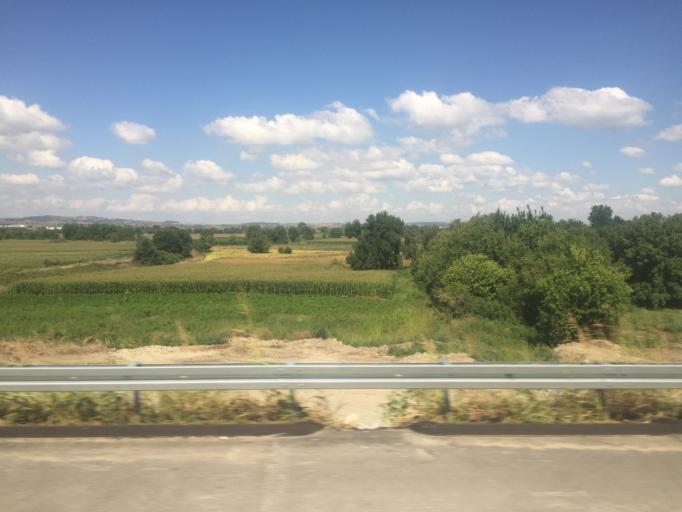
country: TR
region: Balikesir
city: Gobel
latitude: 40.0248
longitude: 28.2083
